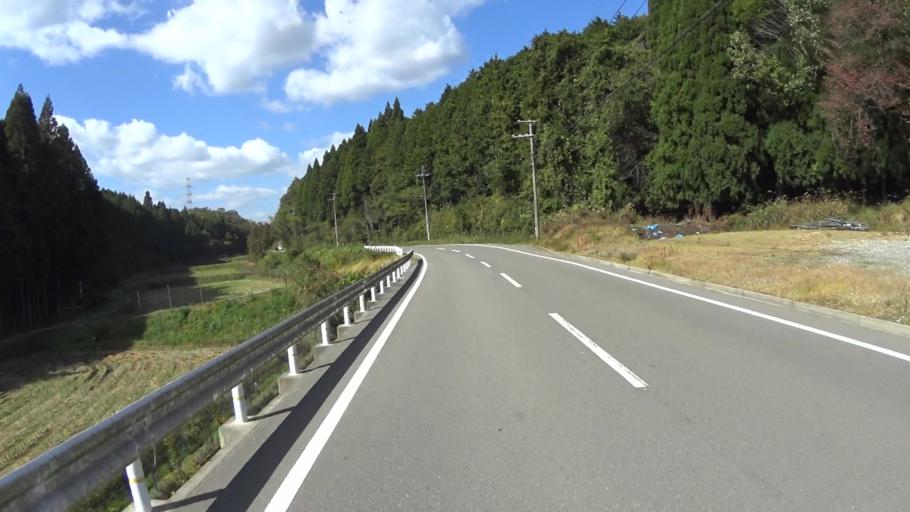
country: JP
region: Kyoto
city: Kameoka
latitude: 35.1616
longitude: 135.4693
